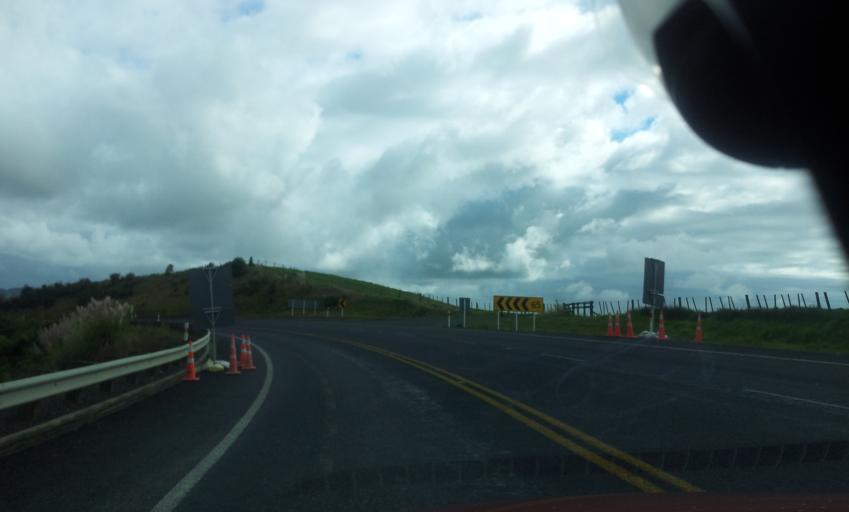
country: NZ
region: Northland
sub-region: Whangarei
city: Ruakaka
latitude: -36.0553
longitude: 174.4257
